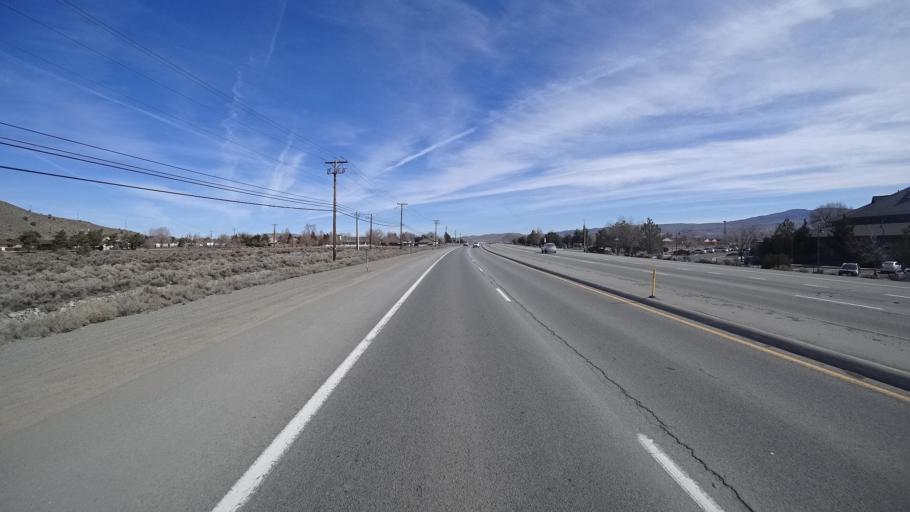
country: US
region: Nevada
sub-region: Washoe County
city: Spanish Springs
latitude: 39.6212
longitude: -119.7257
